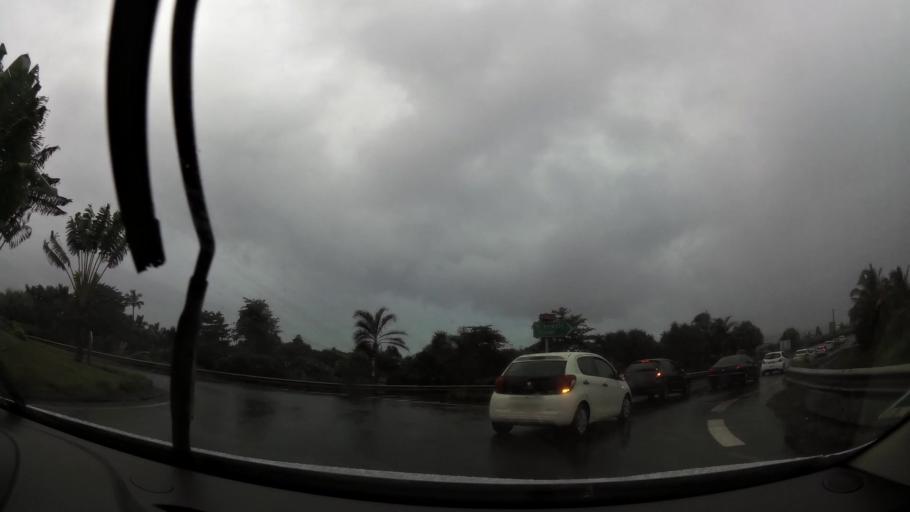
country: RE
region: Reunion
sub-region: Reunion
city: Saint-Benoit
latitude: -21.0264
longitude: 55.7049
